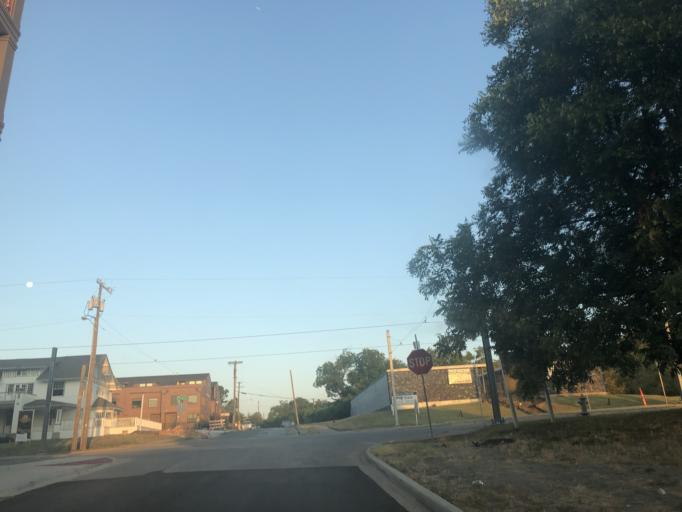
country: US
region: Texas
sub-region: Dallas County
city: Dallas
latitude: 32.7507
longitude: -96.8237
